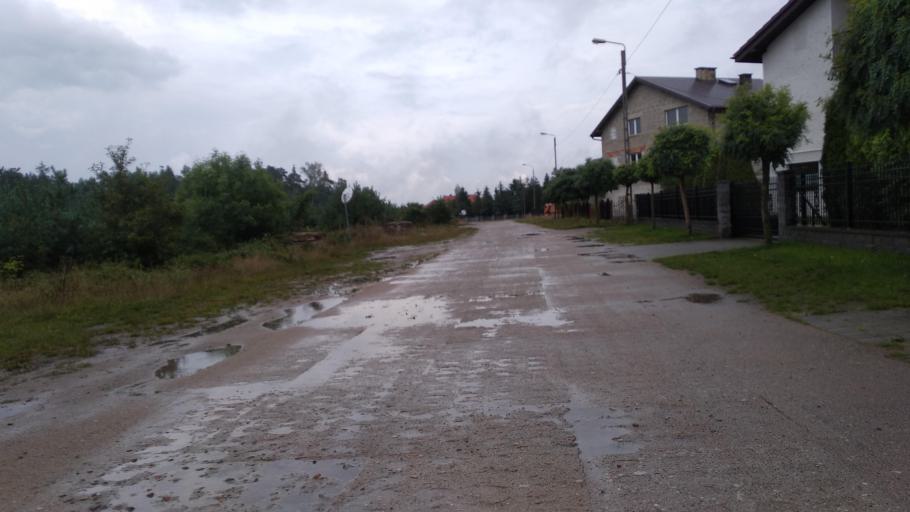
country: PL
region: Pomeranian Voivodeship
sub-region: Powiat wejherowski
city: Bolszewo
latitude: 54.6199
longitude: 18.1634
